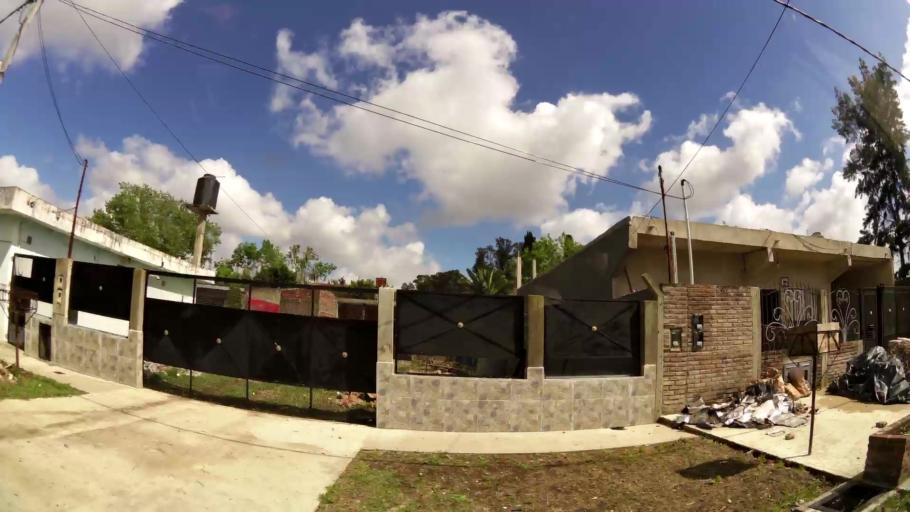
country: AR
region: Buenos Aires
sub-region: Partido de Quilmes
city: Quilmes
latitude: -34.8291
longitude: -58.1748
